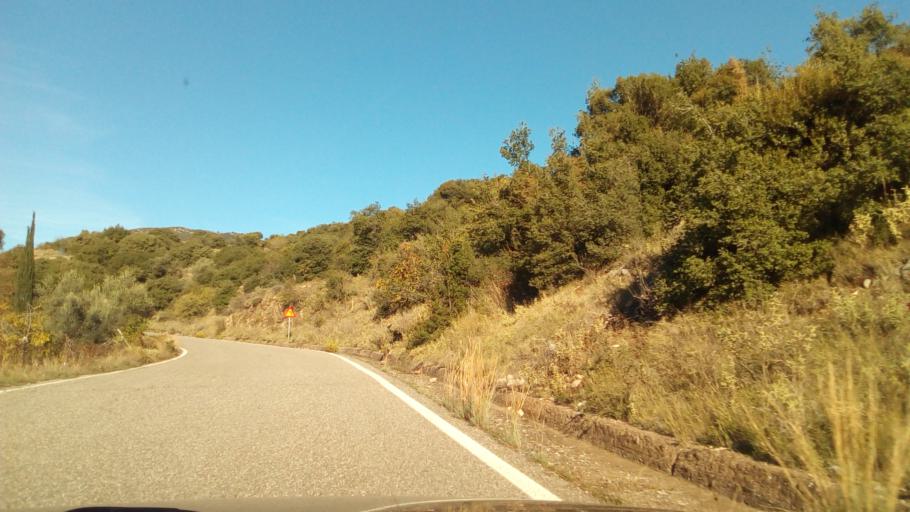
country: GR
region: West Greece
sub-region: Nomos Aitolias kai Akarnanias
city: Nafpaktos
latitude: 38.4842
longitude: 21.8548
